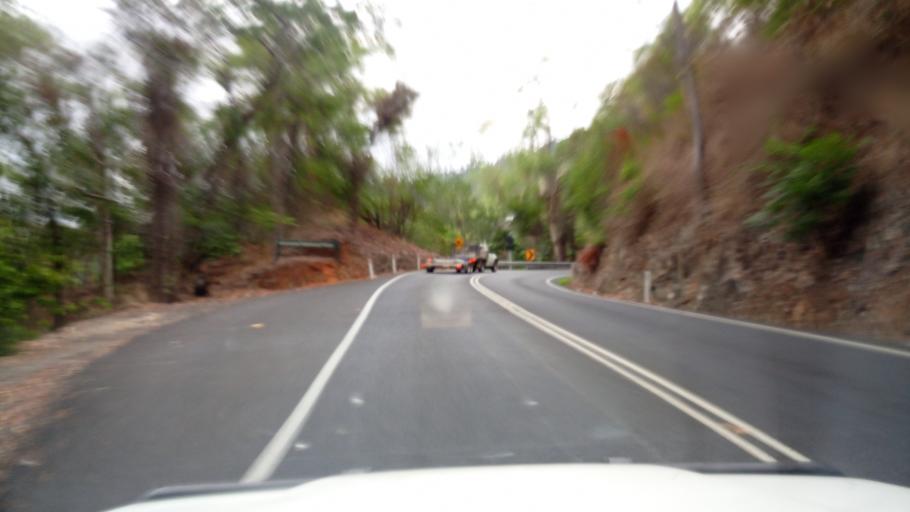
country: AU
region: Queensland
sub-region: Cairns
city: Redlynch
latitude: -16.8404
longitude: 145.6833
